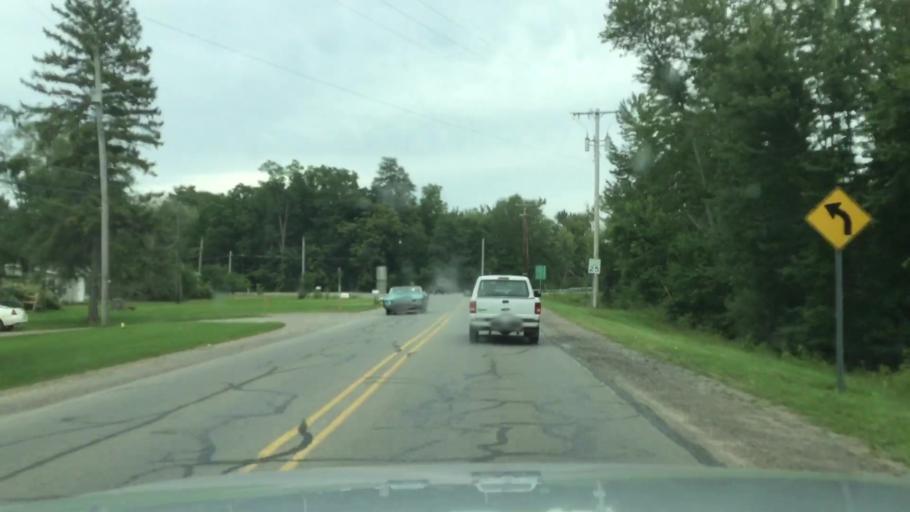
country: US
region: Michigan
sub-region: Genesee County
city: Argentine
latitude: 42.8193
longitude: -83.9430
